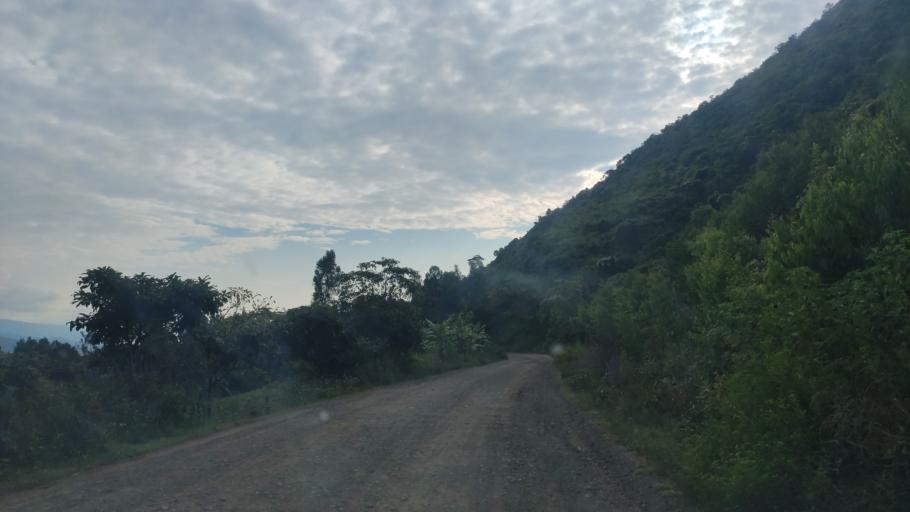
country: ET
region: Southern Nations, Nationalities, and People's Region
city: Arba Minch'
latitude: 6.4431
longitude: 37.3931
